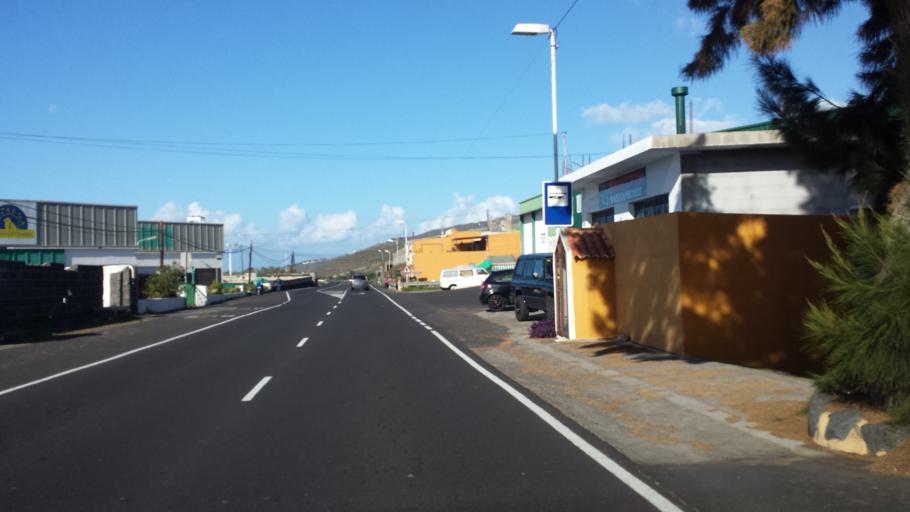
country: ES
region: Canary Islands
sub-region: Provincia de Santa Cruz de Tenerife
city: Los Llanos de Aridane
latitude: 28.6424
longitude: -17.9098
